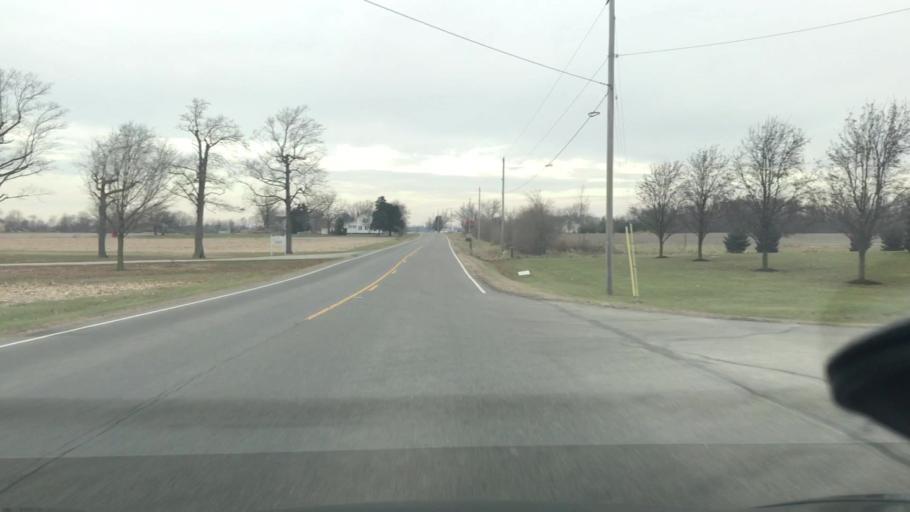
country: US
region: Ohio
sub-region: Madison County
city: London
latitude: 39.8330
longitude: -83.3728
